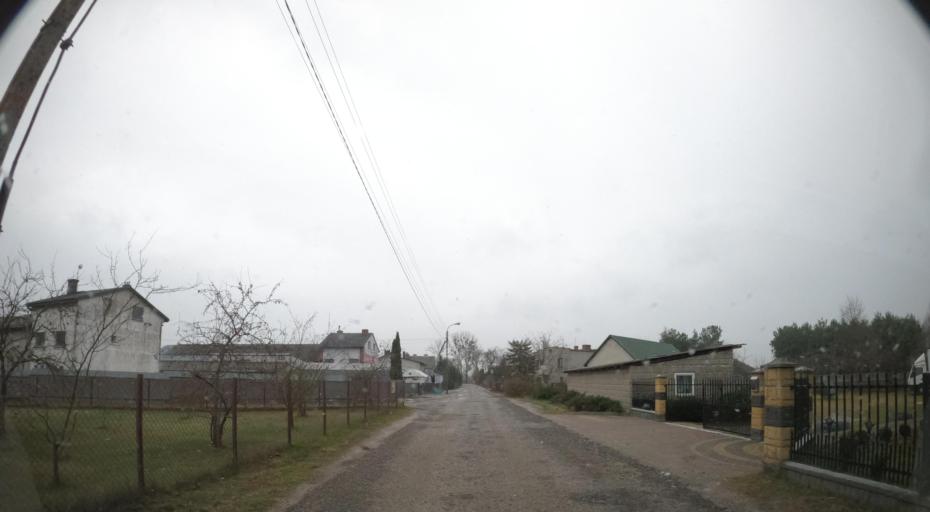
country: PL
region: Masovian Voivodeship
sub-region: Powiat radomski
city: Jedlnia-Letnisko
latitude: 51.3974
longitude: 21.2729
